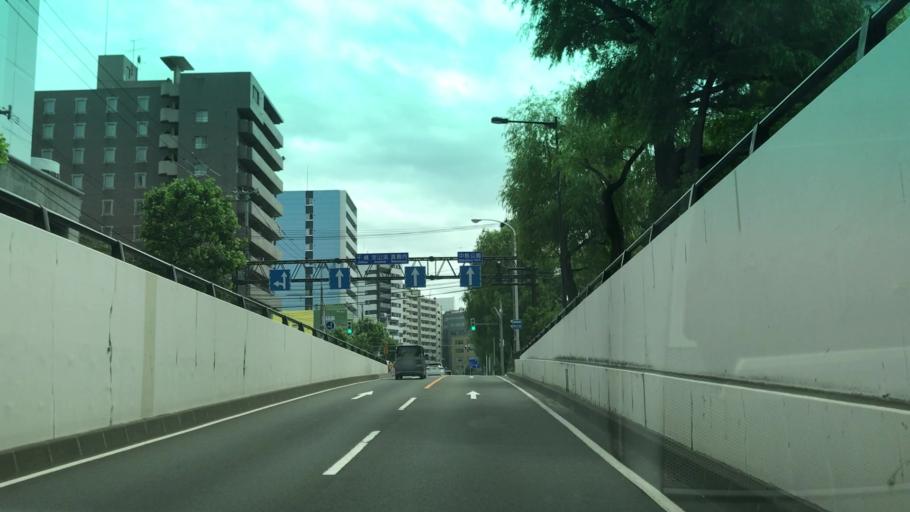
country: JP
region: Hokkaido
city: Sapporo
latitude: 43.0557
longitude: 141.3585
